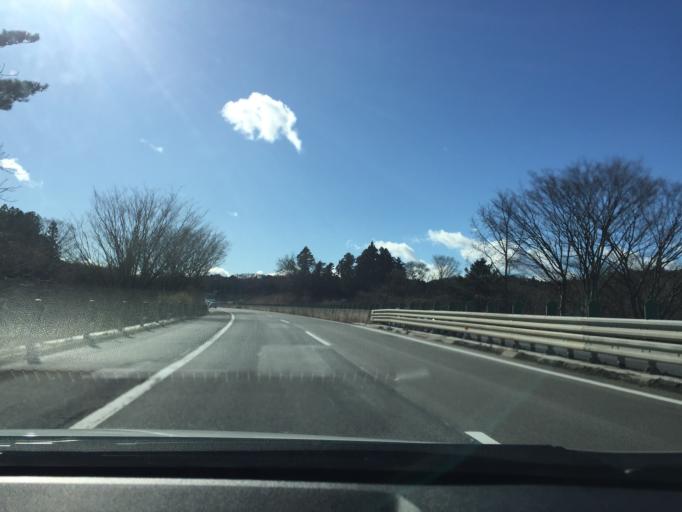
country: JP
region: Fukushima
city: Nihommatsu
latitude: 37.6182
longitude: 140.4236
